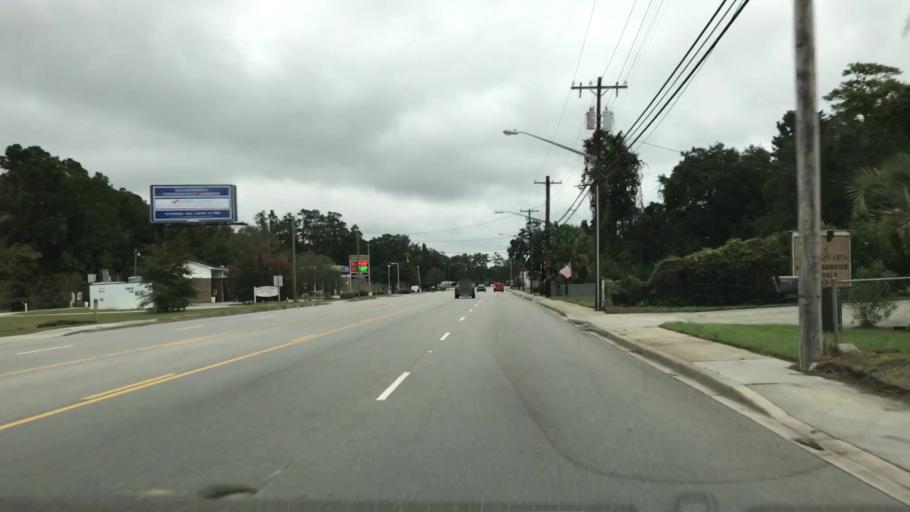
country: US
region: South Carolina
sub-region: Georgetown County
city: Georgetown
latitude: 33.3470
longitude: -79.2959
